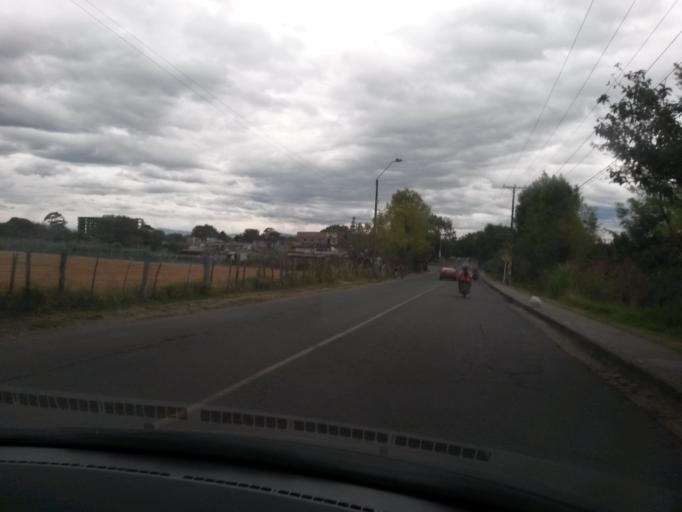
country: CO
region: Cauca
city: Popayan
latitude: 2.4584
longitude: -76.5982
